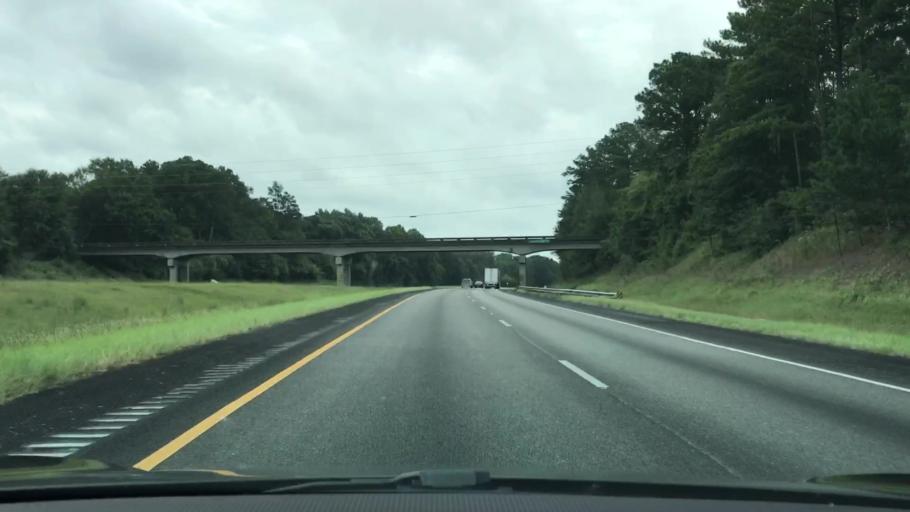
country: US
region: Alabama
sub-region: Elmore County
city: Tallassee
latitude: 32.4367
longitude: -85.8736
